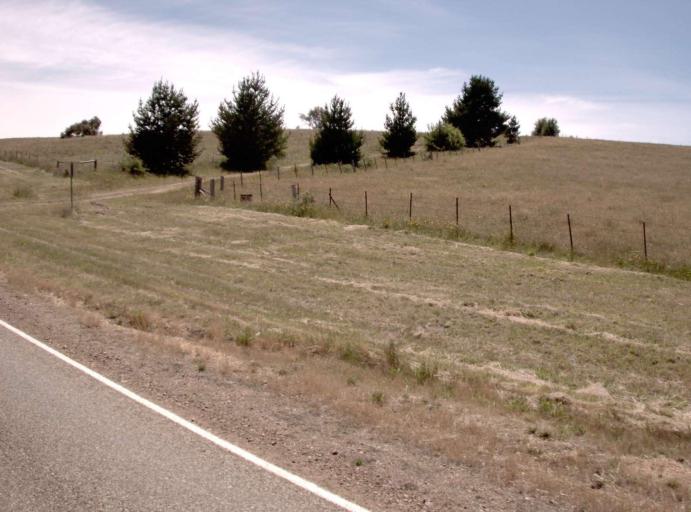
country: AU
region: Victoria
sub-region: Alpine
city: Mount Beauty
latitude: -37.0083
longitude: 147.6598
